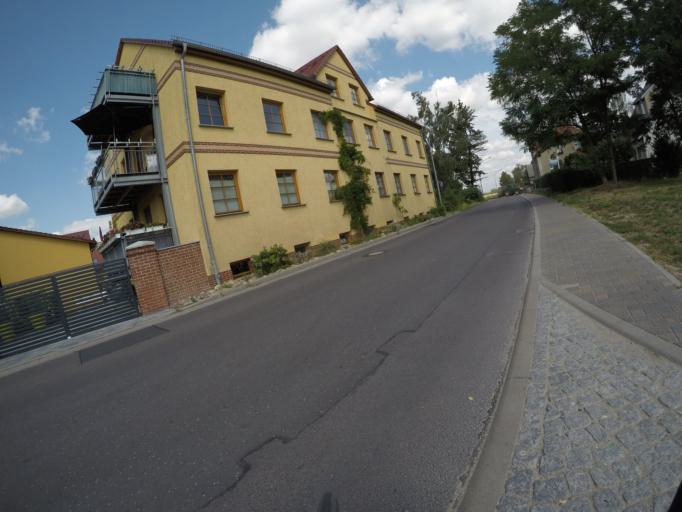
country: DE
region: Brandenburg
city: Werder
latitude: 52.4105
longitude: 12.9646
